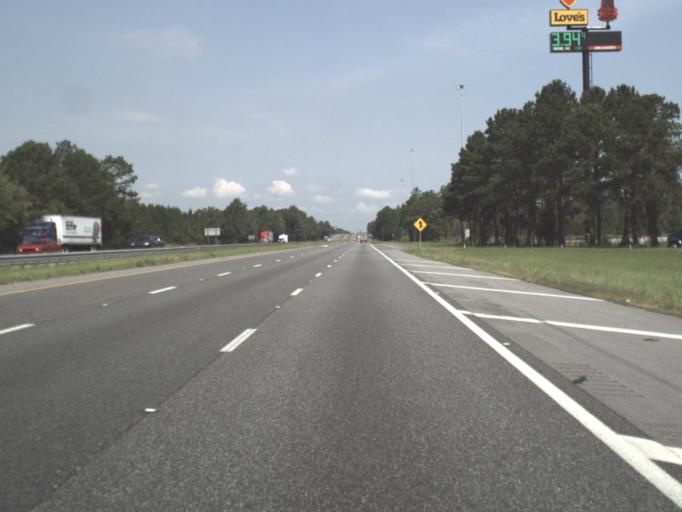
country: US
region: Florida
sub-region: Hamilton County
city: Jasper
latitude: 30.4499
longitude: -82.9347
